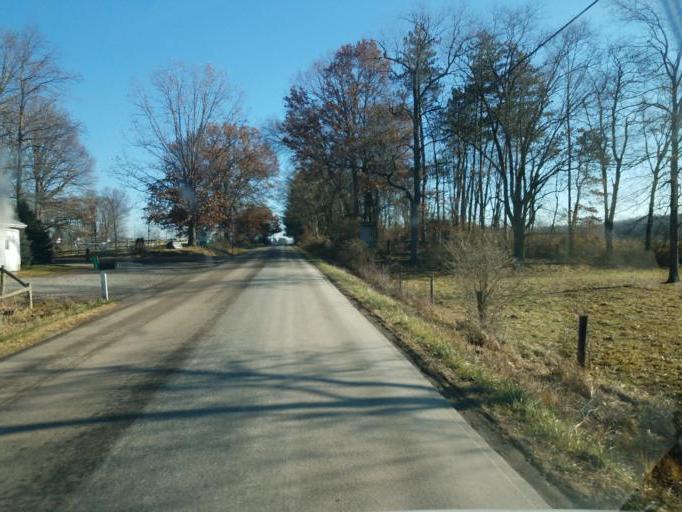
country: US
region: Ohio
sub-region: Wayne County
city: Apple Creek
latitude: 40.6750
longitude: -81.8330
